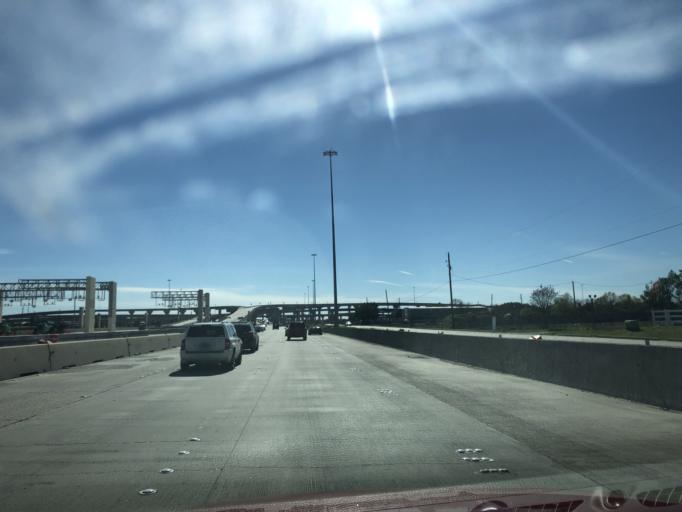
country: US
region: Texas
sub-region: Brazoria County
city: Brookside Village
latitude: 29.6057
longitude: -95.3872
